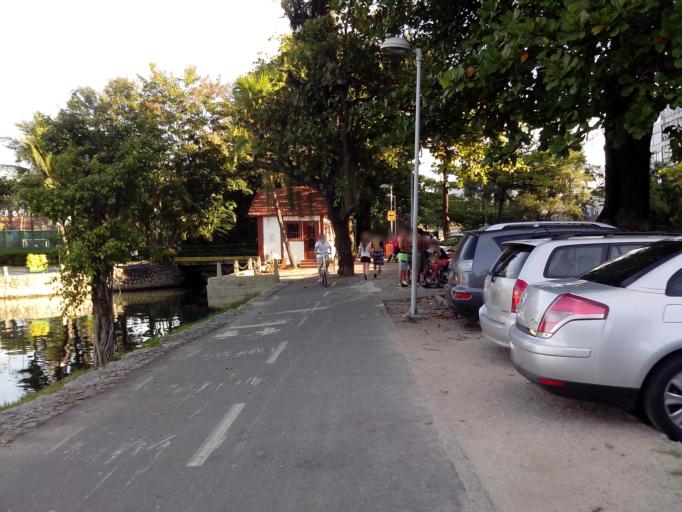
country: BR
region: Rio de Janeiro
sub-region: Rio De Janeiro
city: Rio de Janeiro
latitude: -22.9663
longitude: -43.2164
